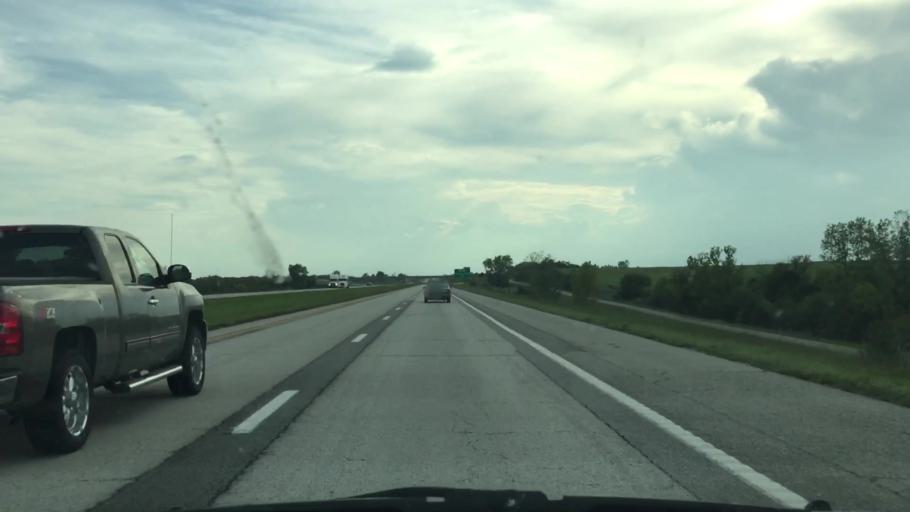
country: US
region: Missouri
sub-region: Harrison County
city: Bethany
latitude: 40.1616
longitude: -94.0284
